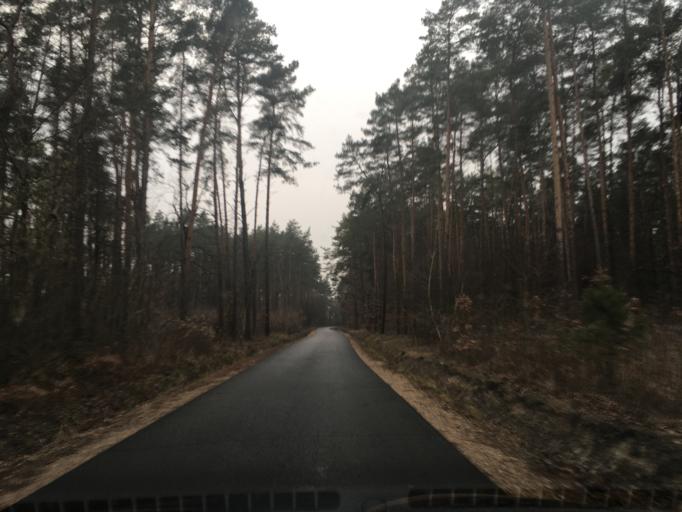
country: PL
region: Masovian Voivodeship
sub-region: Powiat piaseczynski
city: Lesznowola
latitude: 52.0792
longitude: 20.9282
